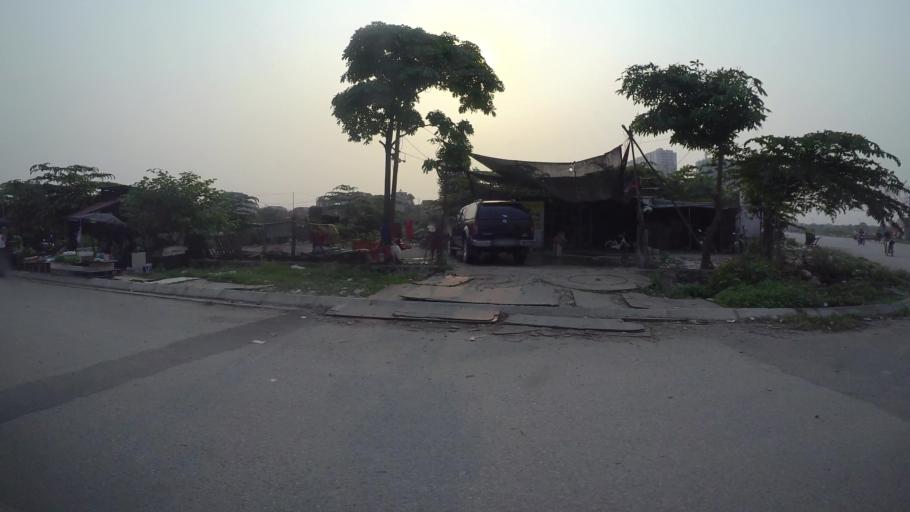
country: VN
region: Ha Noi
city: Cau Dien
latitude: 21.0068
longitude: 105.7266
